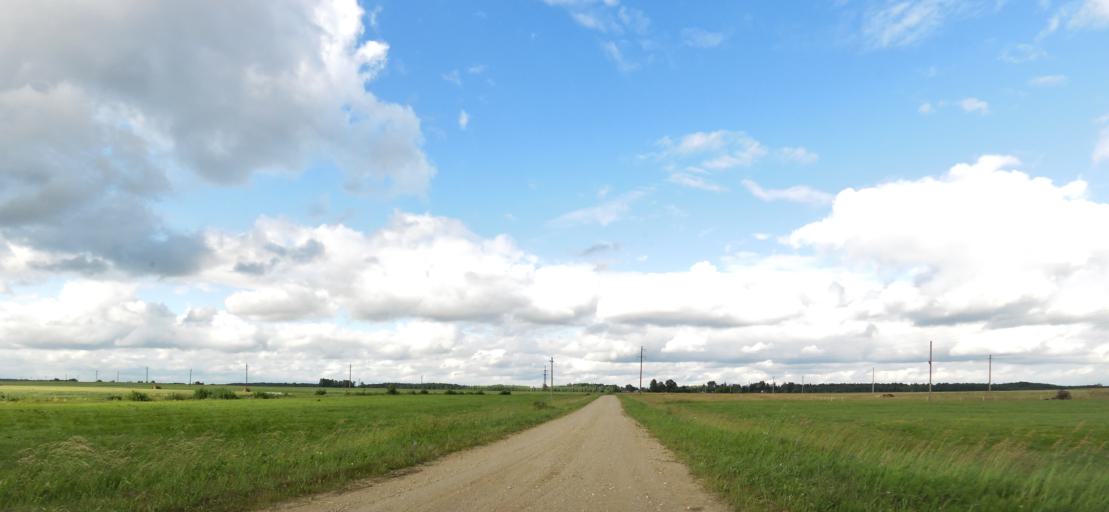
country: LT
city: Obeliai
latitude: 55.9009
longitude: 25.1898
